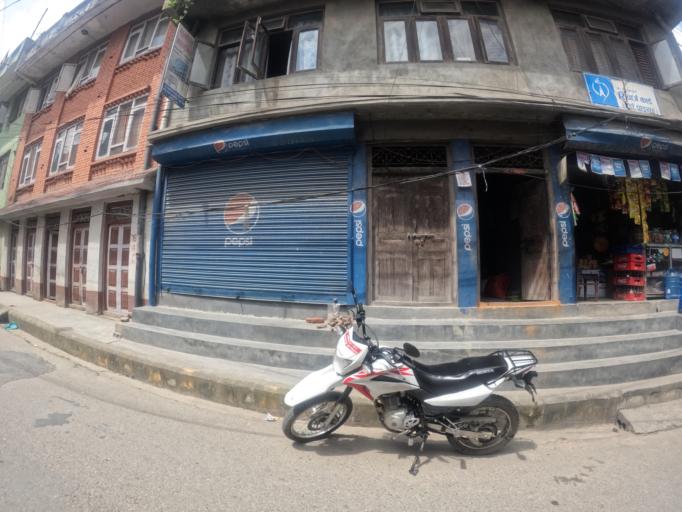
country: NP
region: Central Region
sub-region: Bagmati Zone
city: Bhaktapur
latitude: 27.6823
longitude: 85.3832
